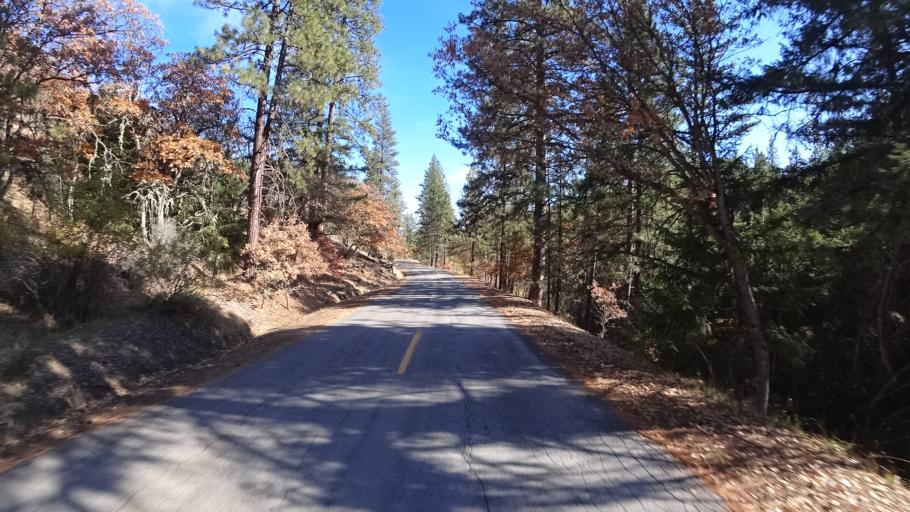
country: US
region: California
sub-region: Siskiyou County
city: Yreka
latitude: 41.7232
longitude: -122.6992
